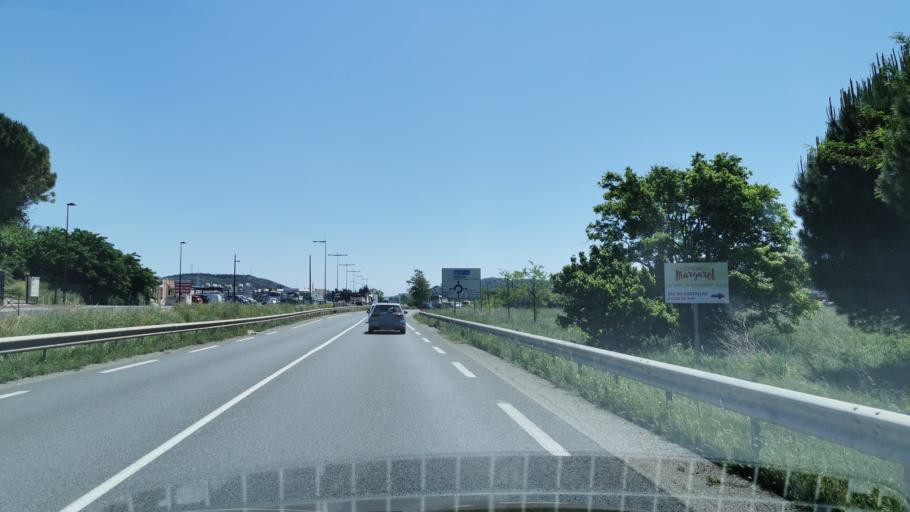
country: FR
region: Languedoc-Roussillon
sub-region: Departement de l'Aude
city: Nevian
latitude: 43.1851
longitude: 2.9302
